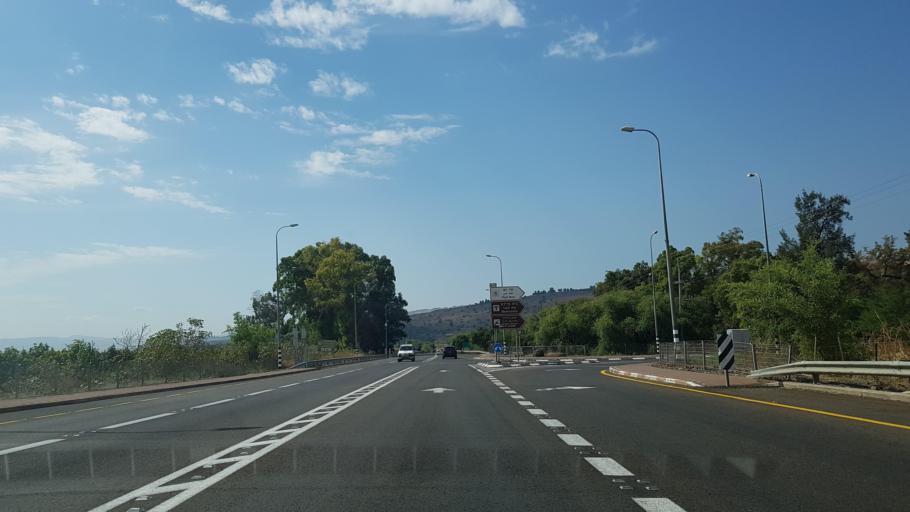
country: SY
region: Quneitra
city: Al Butayhah
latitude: 32.9042
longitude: 35.6348
